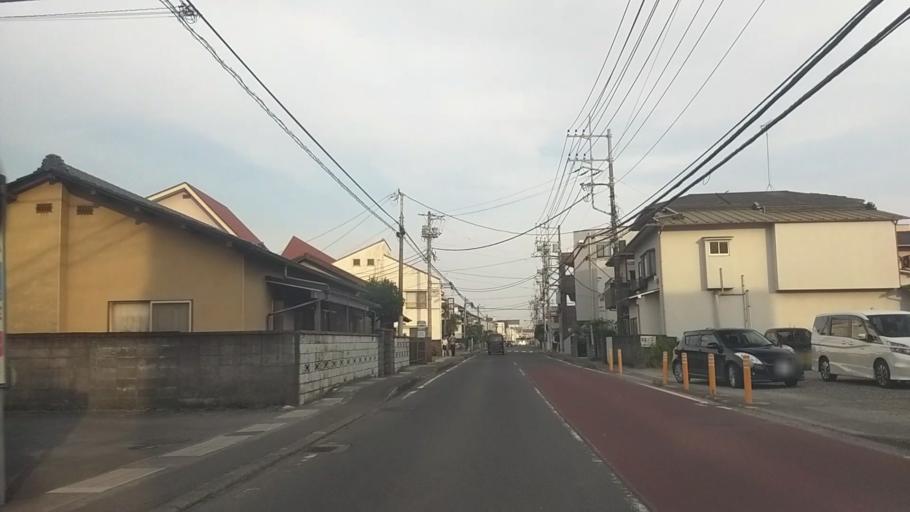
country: JP
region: Kanagawa
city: Odawara
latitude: 35.2755
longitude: 139.1558
